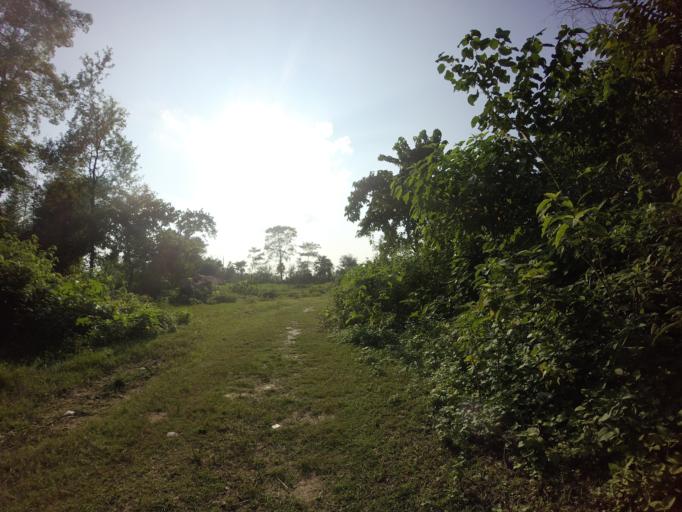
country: NP
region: Far Western
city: Tikapur
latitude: 28.4430
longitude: 81.0782
